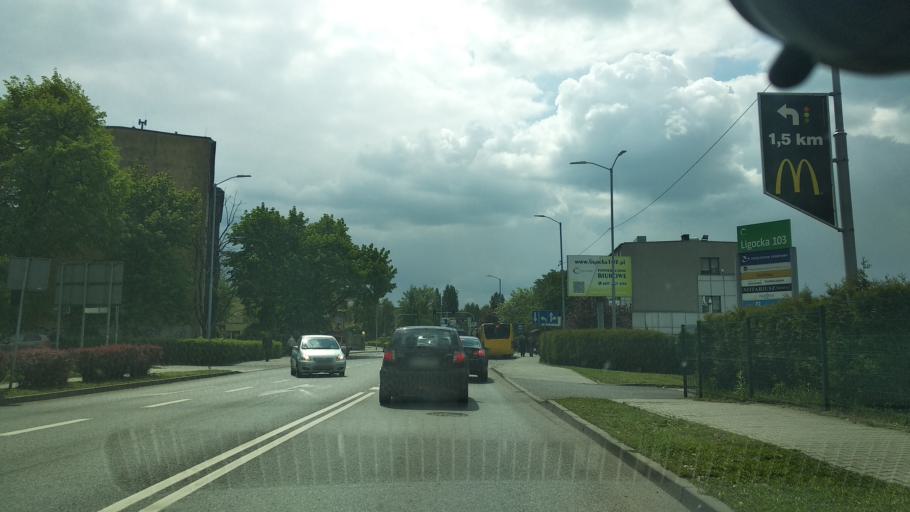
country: PL
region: Silesian Voivodeship
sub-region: Katowice
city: Katowice
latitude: 50.2352
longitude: 18.9780
